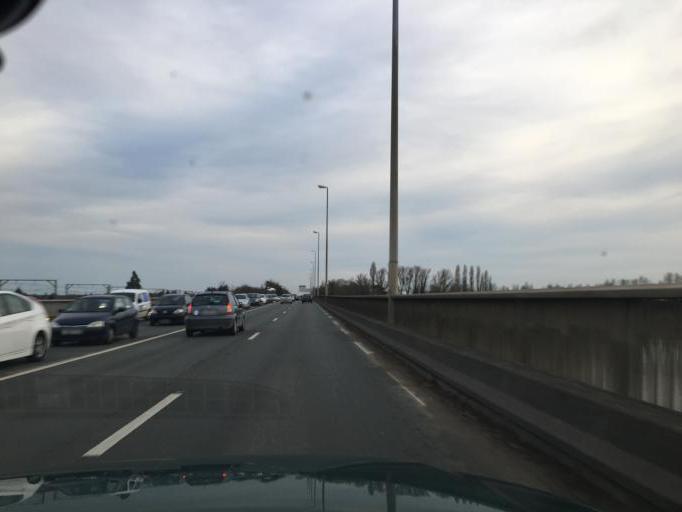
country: FR
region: Centre
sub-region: Departement du Loiret
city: Saint-Jean-le-Blanc
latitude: 47.8982
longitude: 1.9204
